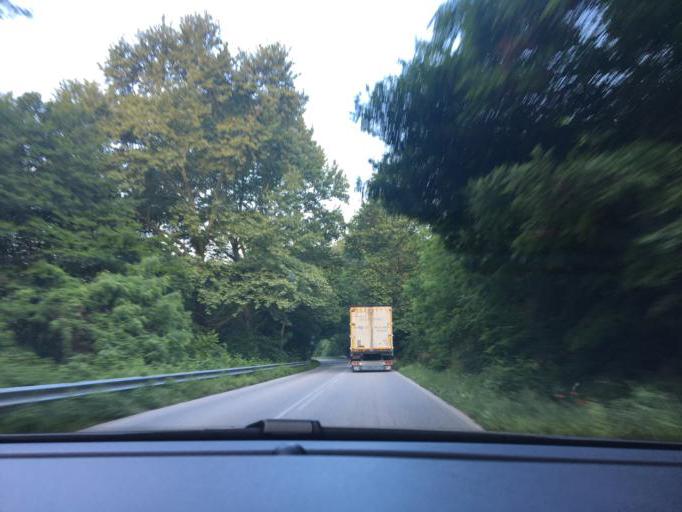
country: BG
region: Blagoevgrad
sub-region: Obshtina Petrich
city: Petrich
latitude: 41.4011
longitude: 23.0837
